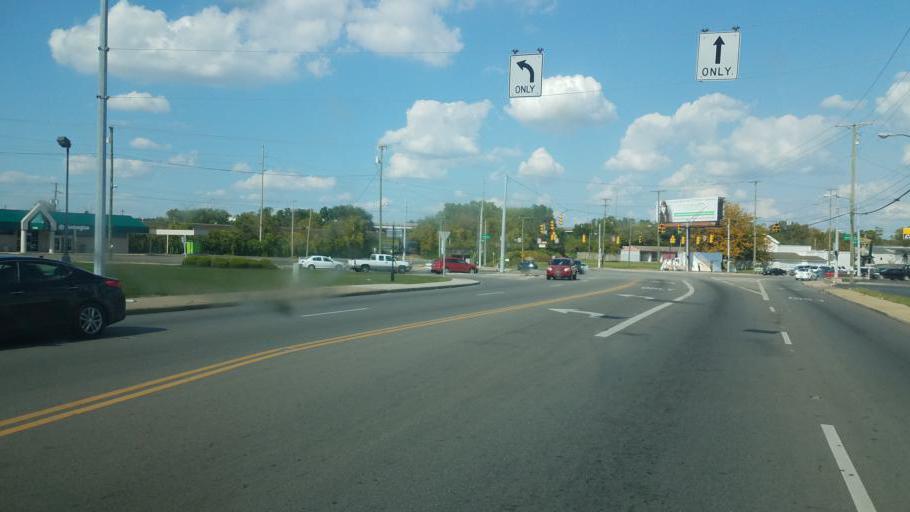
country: US
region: Ohio
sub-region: Franklin County
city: Grandview Heights
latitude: 39.9449
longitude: -83.0363
